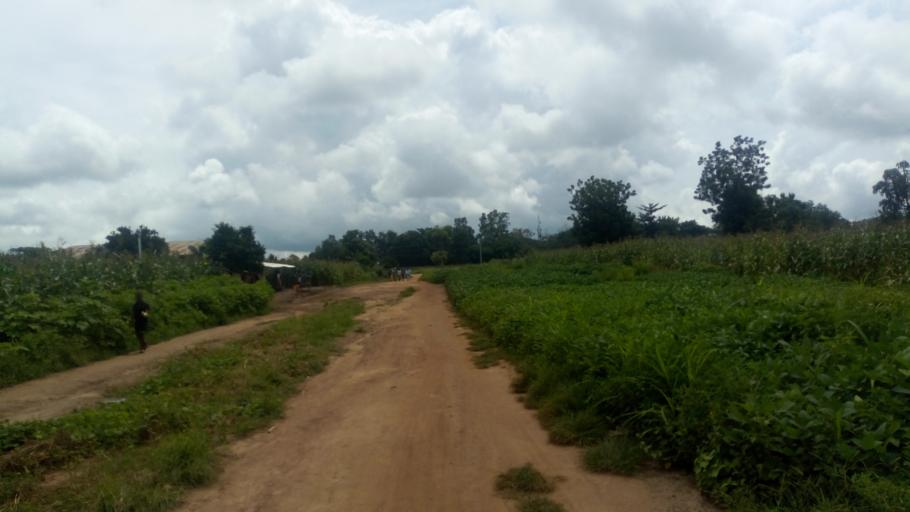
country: TG
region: Centrale
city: Sotouboua
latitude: 8.5560
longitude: 0.9941
